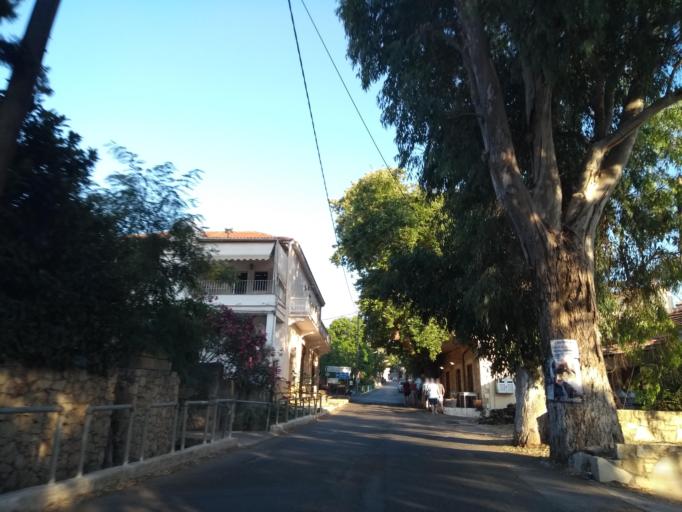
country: GR
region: Crete
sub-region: Nomos Chanias
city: Kalivai
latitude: 35.4092
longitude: 24.1974
